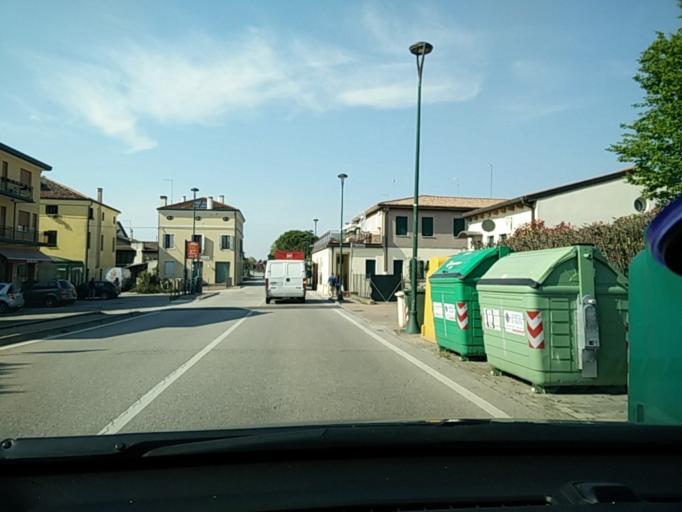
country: IT
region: Veneto
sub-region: Provincia di Venezia
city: Dese
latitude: 45.5279
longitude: 12.3043
